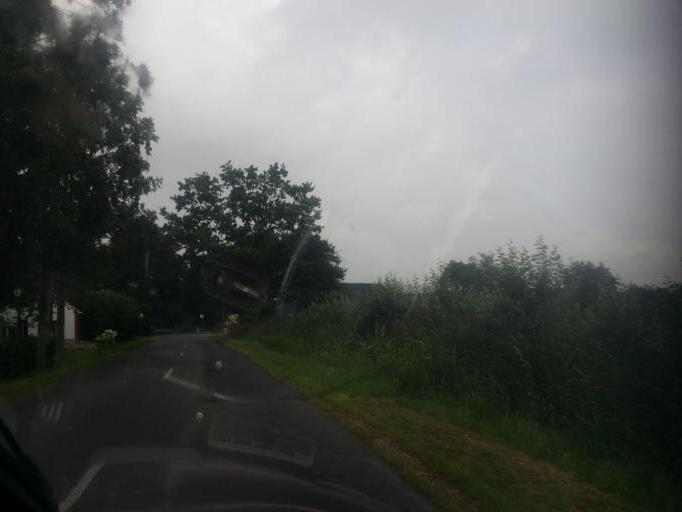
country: DE
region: Schleswig-Holstein
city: Norderheistedt
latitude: 54.2490
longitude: 9.1487
